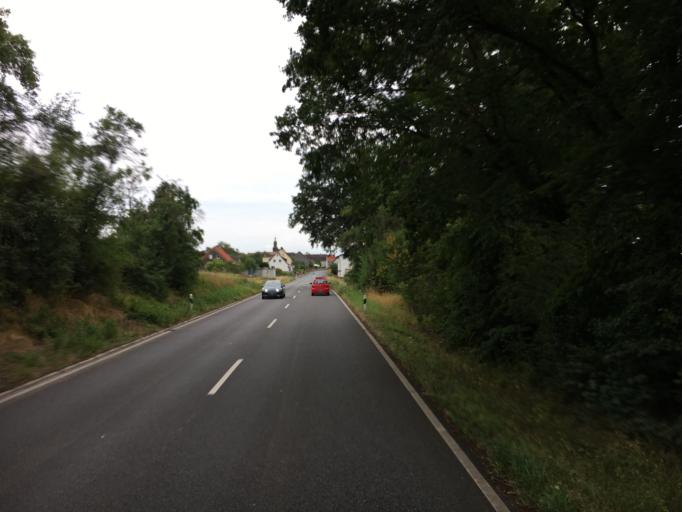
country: DE
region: Hesse
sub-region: Regierungsbezirk Giessen
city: Colbe
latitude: 50.8466
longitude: 8.8576
